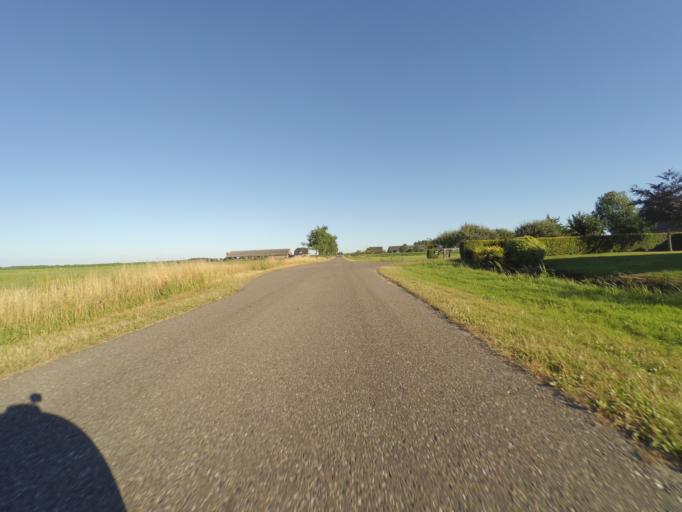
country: NL
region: North Holland
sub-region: Gemeente Wijdemeren
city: Nieuw-Loosdrecht
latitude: 52.1650
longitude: 5.1505
